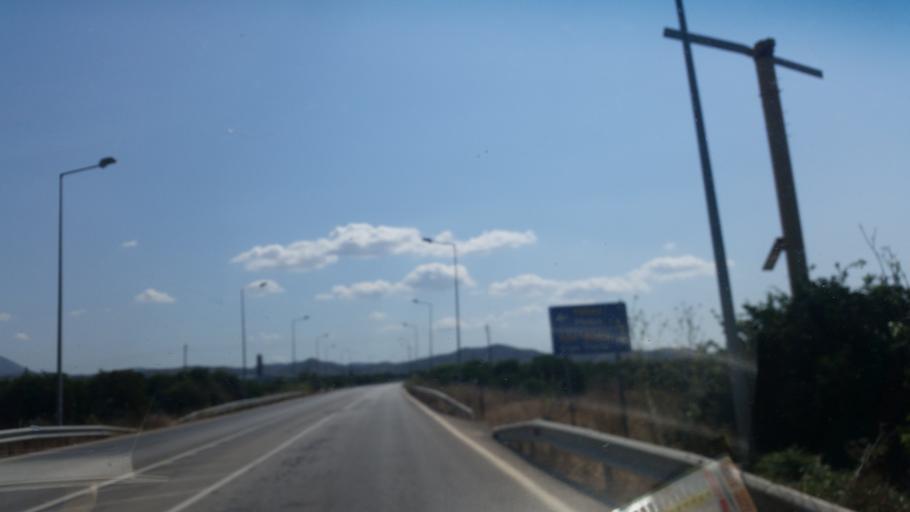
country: GR
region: Peloponnese
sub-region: Nomos Argolidos
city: Ayia Trias
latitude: 37.6428
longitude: 22.8118
